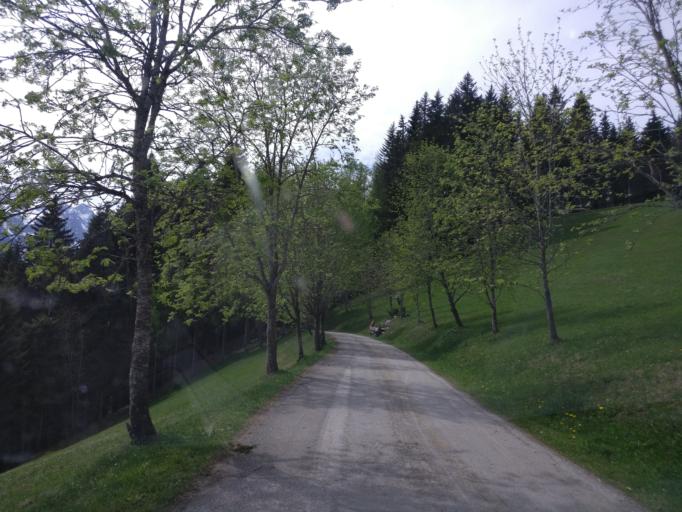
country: AT
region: Salzburg
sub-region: Politischer Bezirk Sankt Johann im Pongau
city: Pfarrwerfen
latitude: 47.4774
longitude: 13.2191
